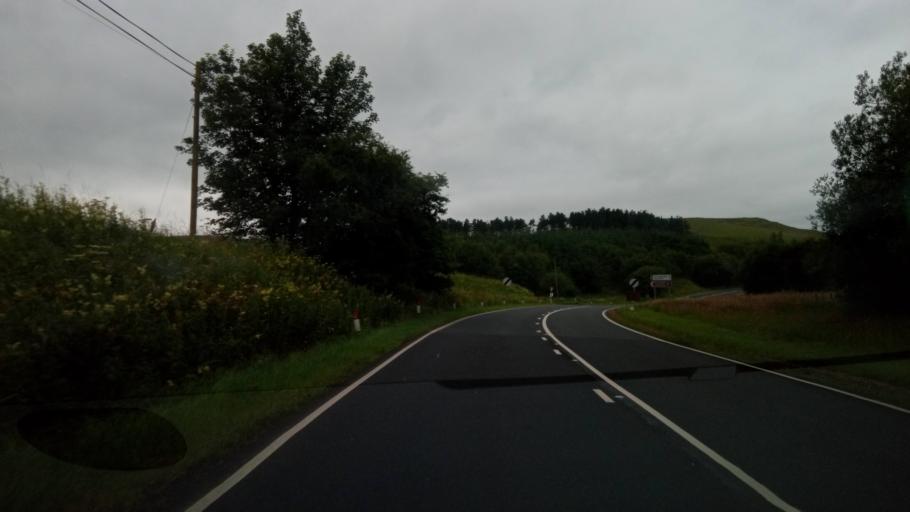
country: GB
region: Scotland
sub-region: The Scottish Borders
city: Hawick
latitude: 55.3609
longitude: -2.8918
